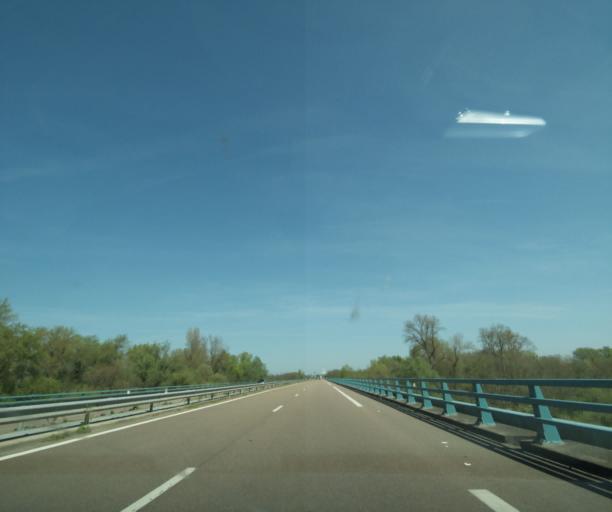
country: FR
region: Bourgogne
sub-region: Departement de la Nievre
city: Sermoise-sur-Loire
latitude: 46.9728
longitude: 3.1955
